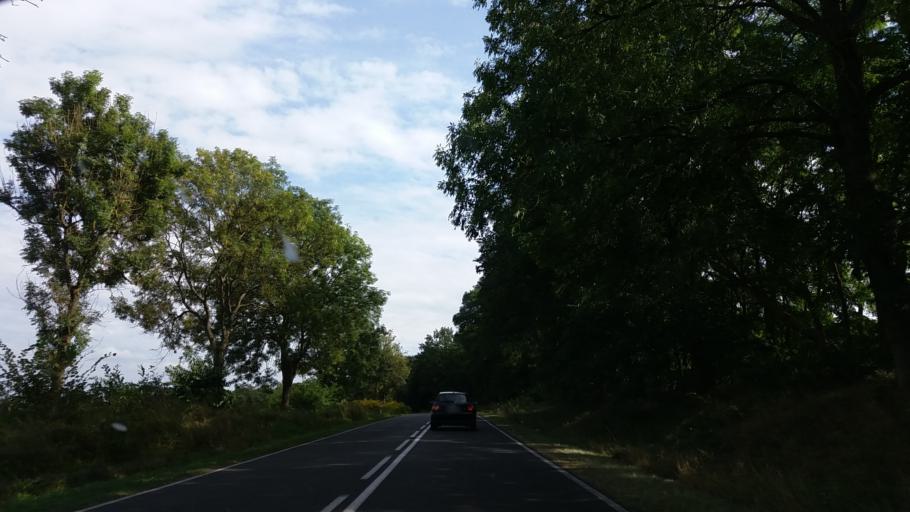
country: PL
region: West Pomeranian Voivodeship
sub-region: Powiat stargardzki
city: Suchan
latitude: 53.2110
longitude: 15.3175
